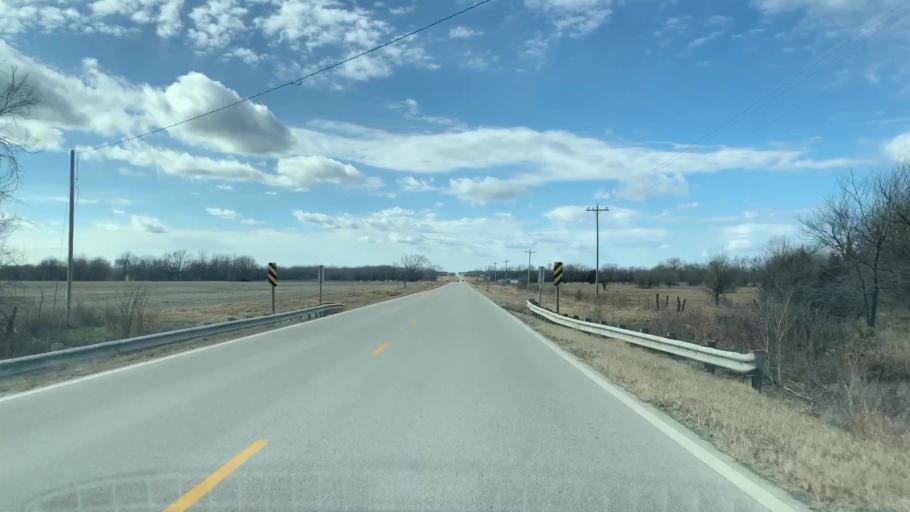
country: US
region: Kansas
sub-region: Neosho County
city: Erie
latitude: 37.5292
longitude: -95.3988
